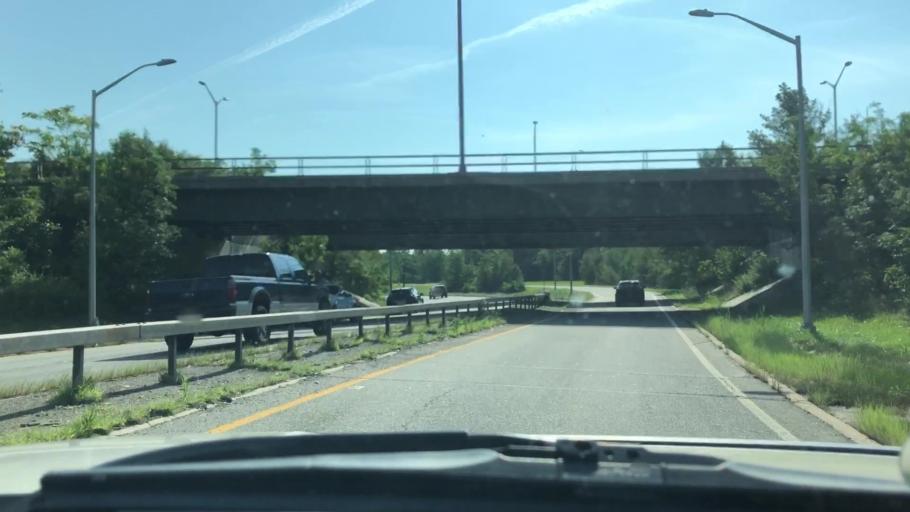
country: US
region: New Jersey
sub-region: Middlesex County
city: Sewaren
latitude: 40.5256
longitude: -74.2241
